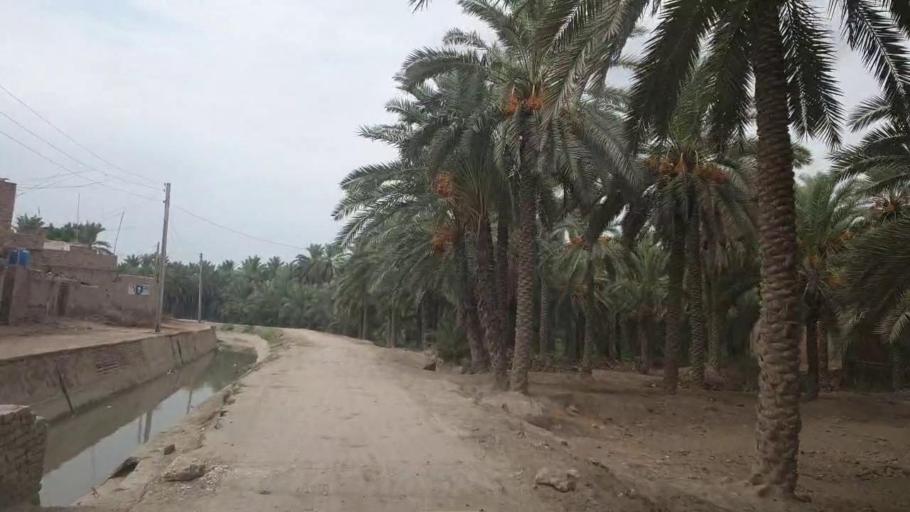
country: PK
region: Sindh
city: Sukkur
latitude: 27.6260
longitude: 68.8082
